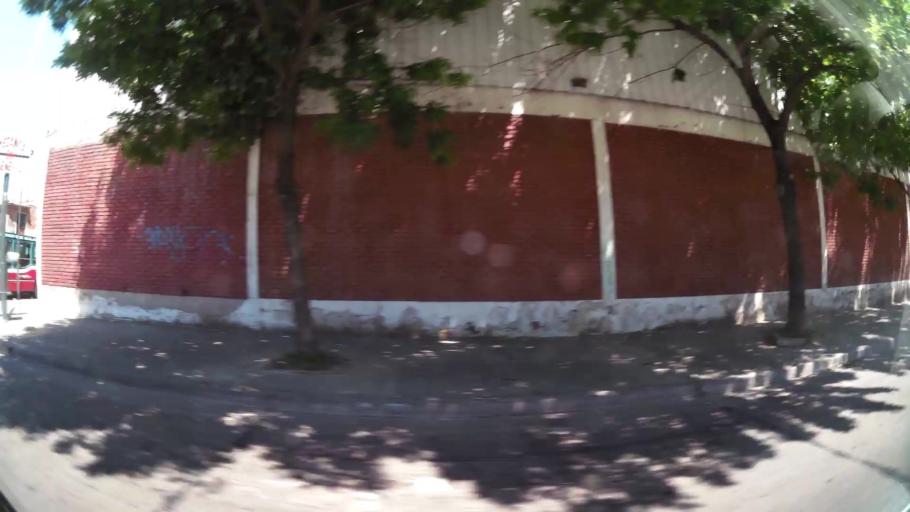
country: AR
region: Buenos Aires
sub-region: Partido de Avellaneda
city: Avellaneda
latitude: -34.6497
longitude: -58.4135
